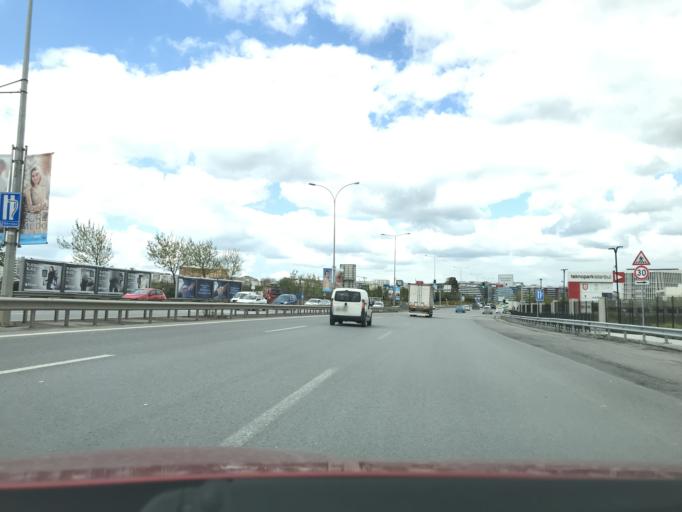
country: TR
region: Istanbul
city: Pendik
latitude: 40.9169
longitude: 29.3119
